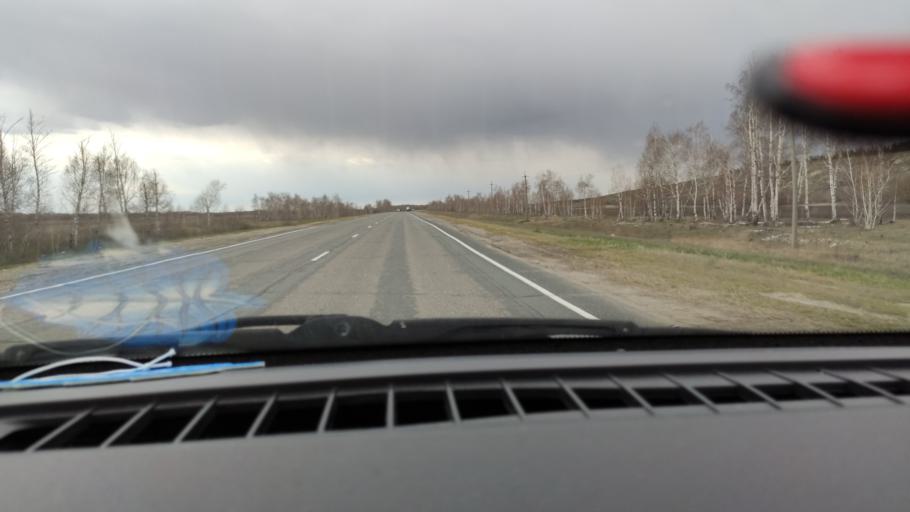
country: RU
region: Saratov
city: Sinodskoye
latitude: 52.0577
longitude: 46.7604
